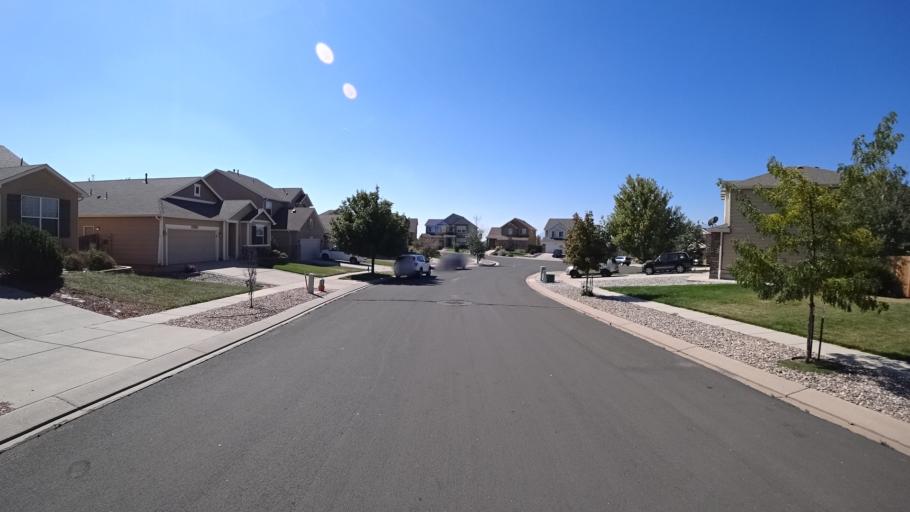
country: US
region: Colorado
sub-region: El Paso County
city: Cimarron Hills
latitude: 38.8972
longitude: -104.6972
